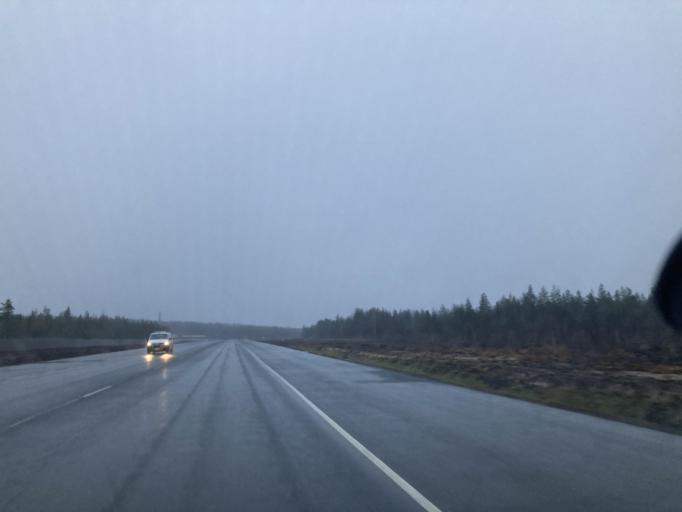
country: FI
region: Lapland
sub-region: Rovaniemi
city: Rovaniemi
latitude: 66.5653
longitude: 25.7962
